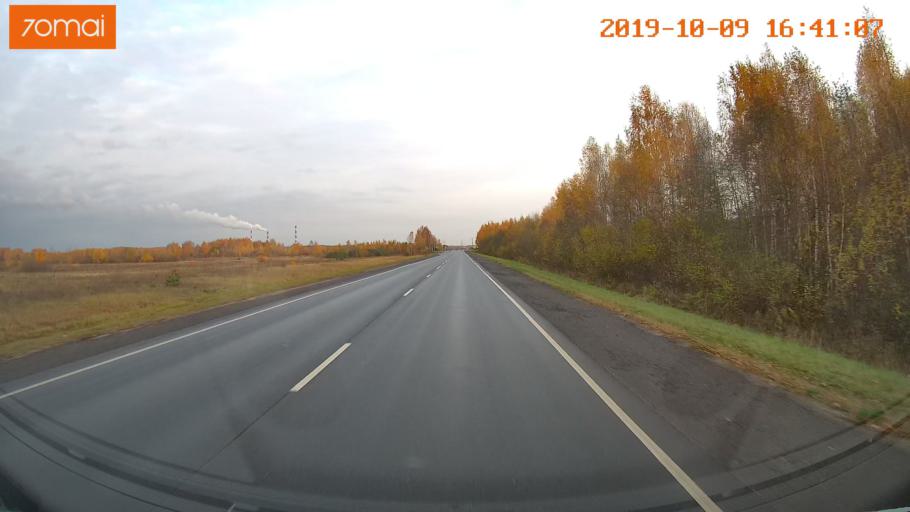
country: RU
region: Kostroma
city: Volgorechensk
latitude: 57.4760
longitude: 41.0743
